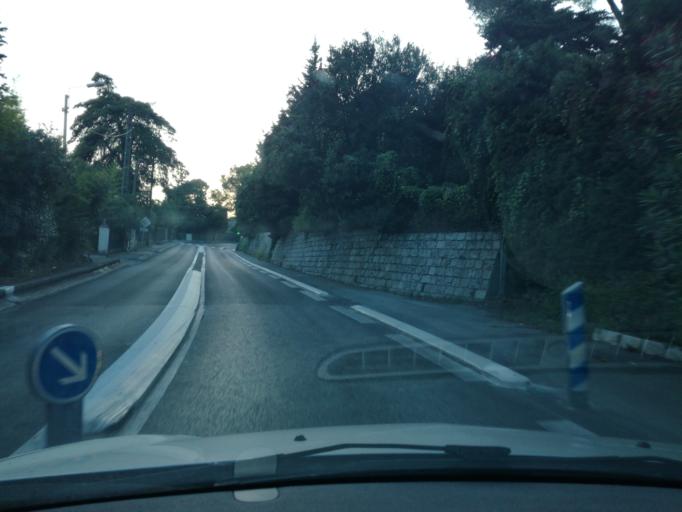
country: FR
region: Provence-Alpes-Cote d'Azur
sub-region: Departement des Alpes-Maritimes
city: Mougins
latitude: 43.5943
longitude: 6.9926
